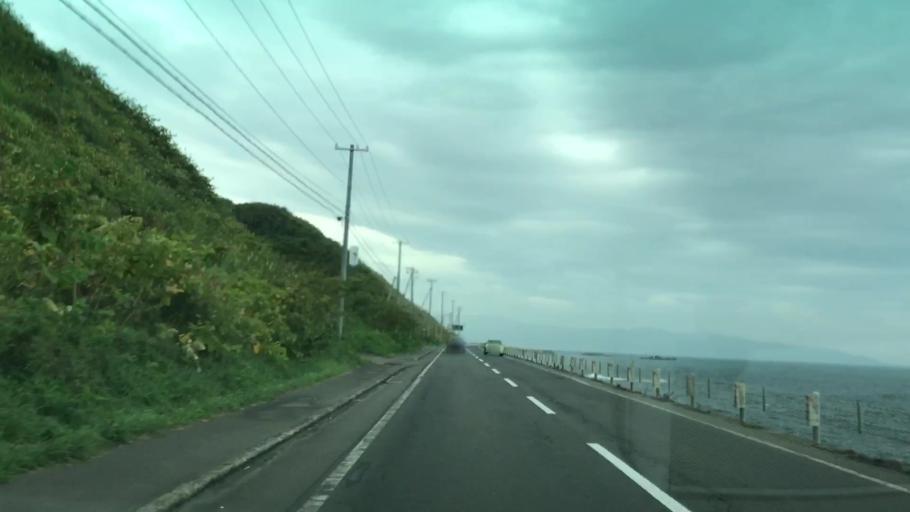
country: JP
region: Hokkaido
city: Iwanai
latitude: 42.8535
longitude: 140.3409
